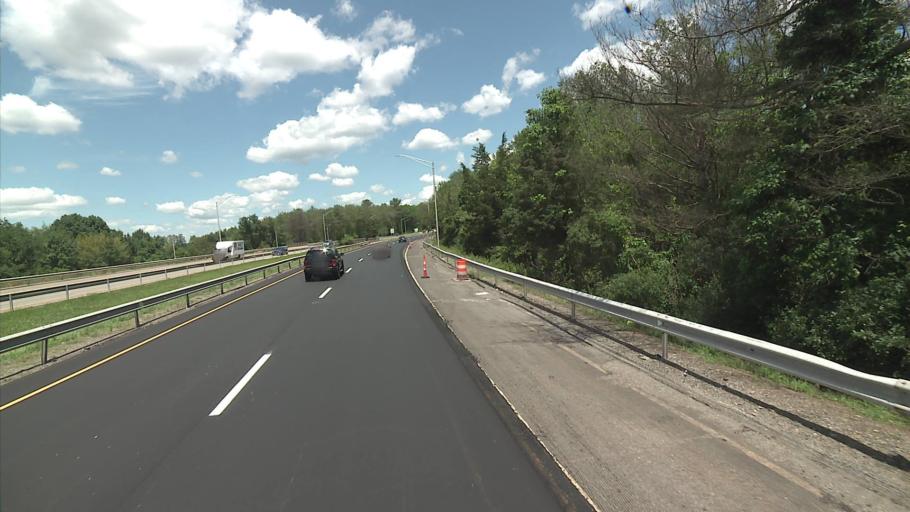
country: US
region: Connecticut
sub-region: Windham County
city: Danielson
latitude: 41.7940
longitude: -71.8766
